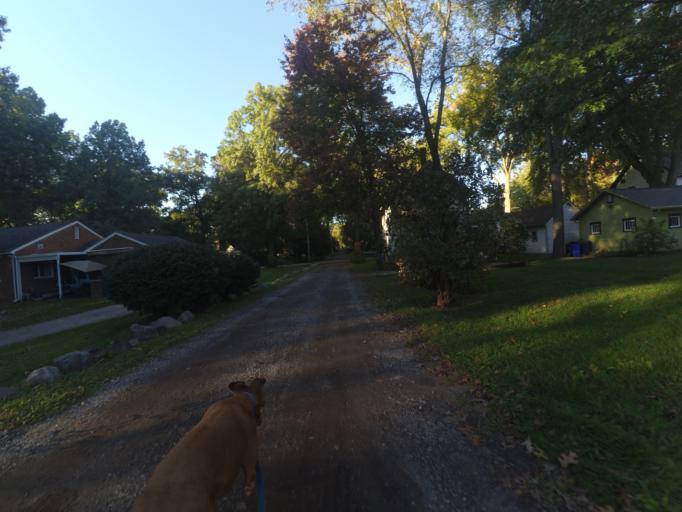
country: US
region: Ohio
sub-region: Portage County
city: Kent
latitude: 41.1520
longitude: -81.3694
